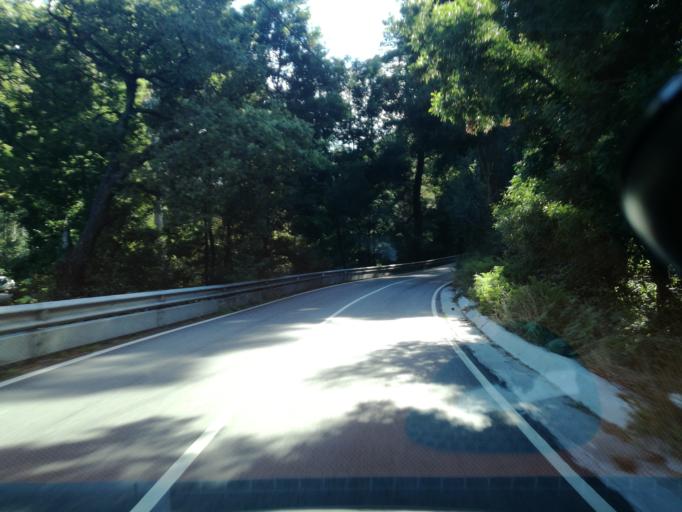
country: PT
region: Porto
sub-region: Santo Tirso
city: Sao Miguel do Couto
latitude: 41.3075
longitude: -8.4474
